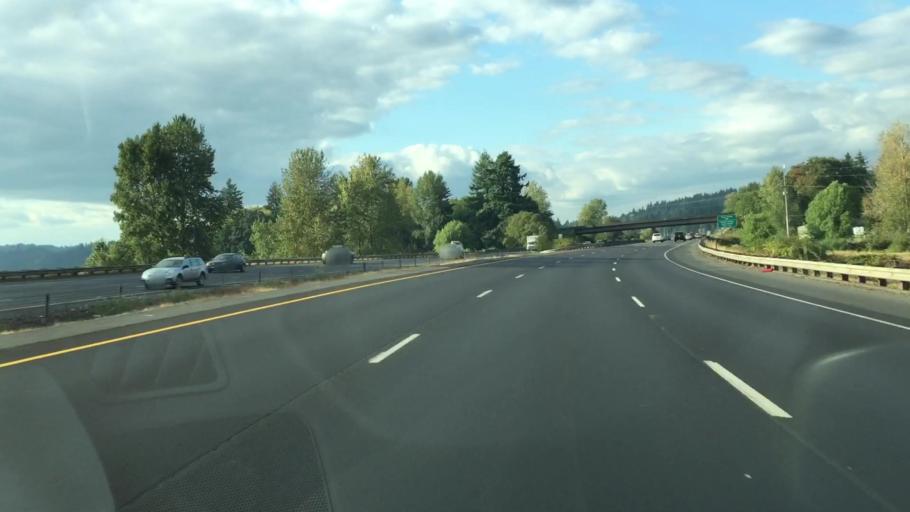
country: US
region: Washington
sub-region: Cowlitz County
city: Kelso
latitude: 46.1305
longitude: -122.8988
